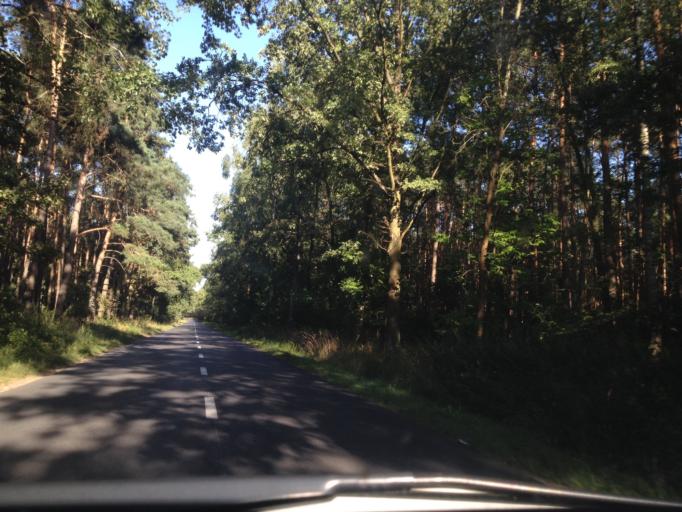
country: PL
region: Greater Poland Voivodeship
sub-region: Powiat sremski
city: Srem
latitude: 52.1058
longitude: 17.0533
